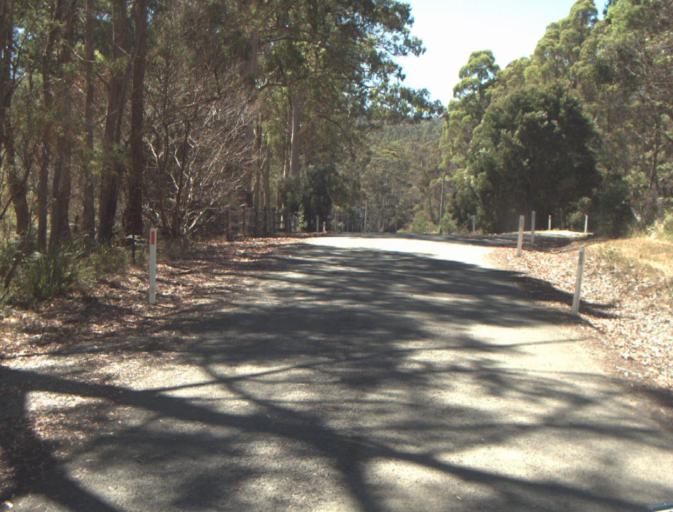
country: AU
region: Tasmania
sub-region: Launceston
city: Newstead
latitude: -41.3435
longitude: 147.3613
